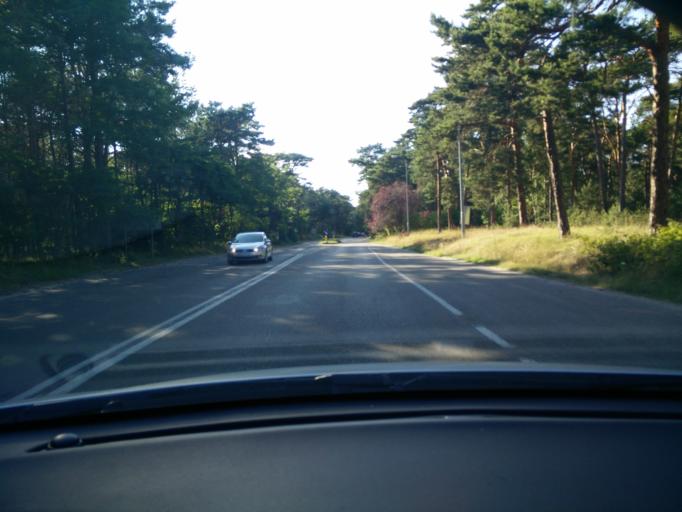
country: PL
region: Pomeranian Voivodeship
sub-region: Powiat pucki
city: Jastarnia
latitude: 54.6729
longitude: 18.7306
